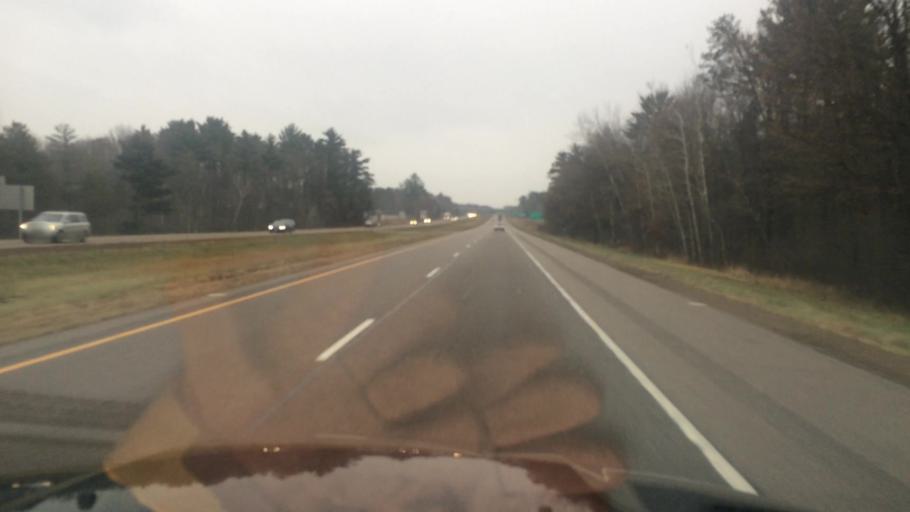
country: US
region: Wisconsin
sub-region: Portage County
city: Stevens Point
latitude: 44.5600
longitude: -89.5902
